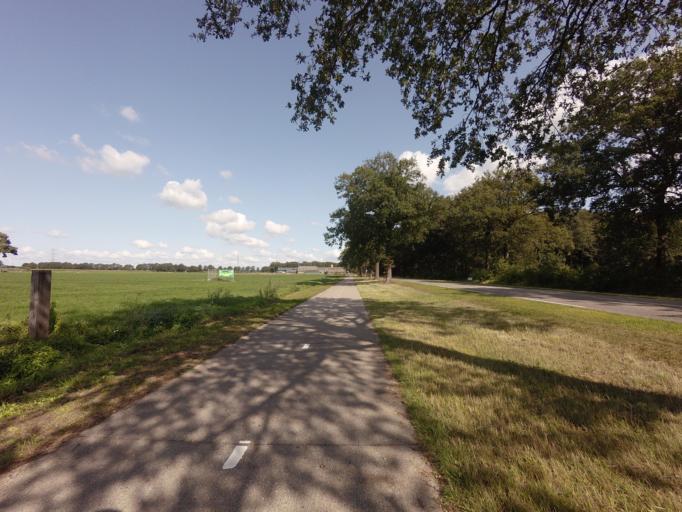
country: NL
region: Overijssel
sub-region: Gemeente Dalfsen
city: Dalfsen
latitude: 52.5349
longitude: 6.2614
